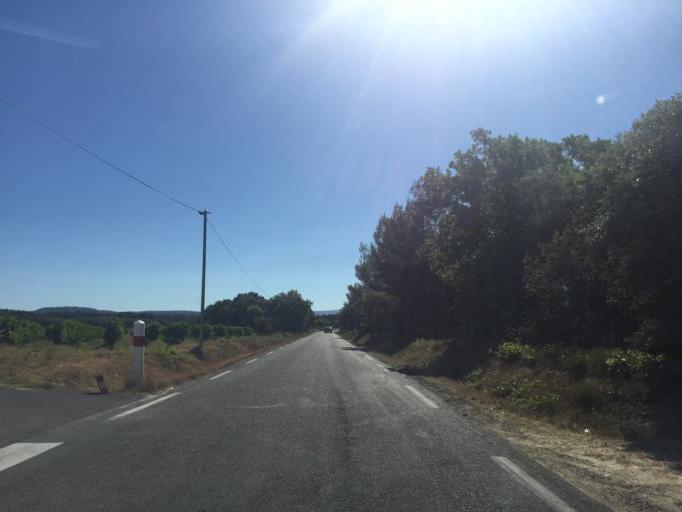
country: FR
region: Provence-Alpes-Cote d'Azur
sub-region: Departement du Vaucluse
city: Saint-Didier
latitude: 44.0255
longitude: 5.1018
